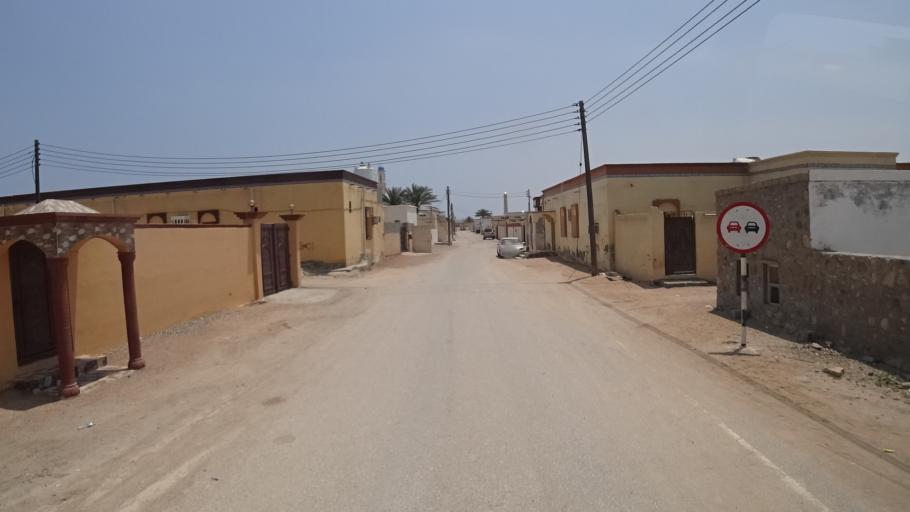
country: OM
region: Ash Sharqiyah
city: Sur
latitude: 22.5142
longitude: 59.7994
